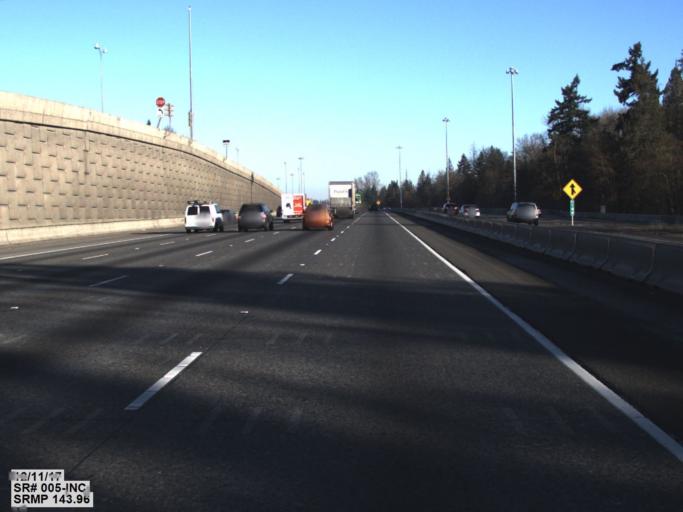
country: US
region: Washington
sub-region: King County
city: Federal Way
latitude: 47.3169
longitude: -122.2965
